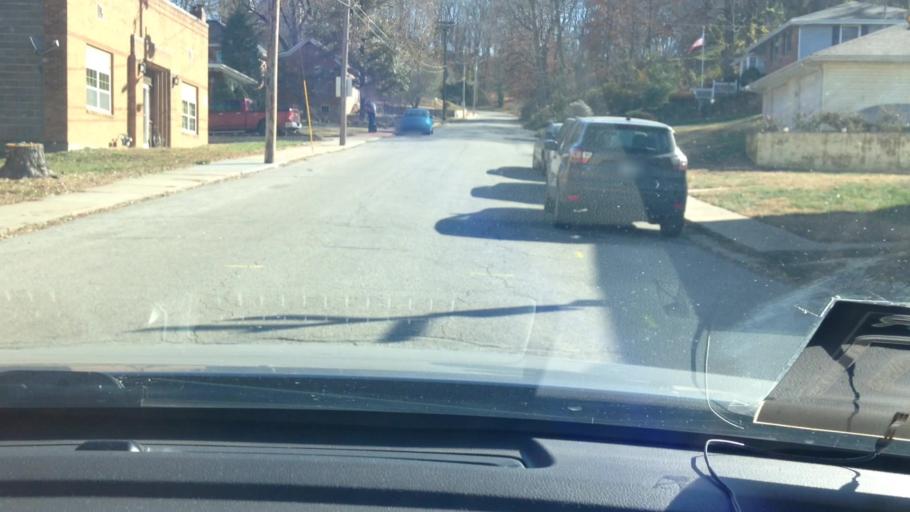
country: US
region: Missouri
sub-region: Platte County
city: Weston
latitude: 39.4100
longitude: -94.9013
